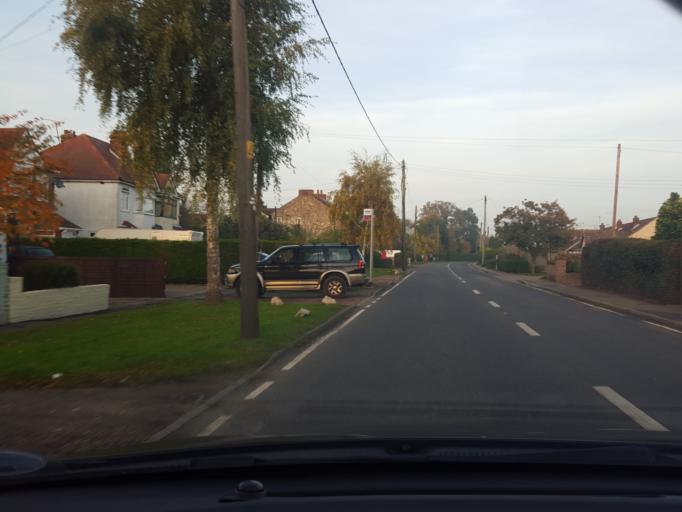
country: GB
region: England
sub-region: Essex
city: Little Clacton
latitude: 51.8381
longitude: 1.1441
